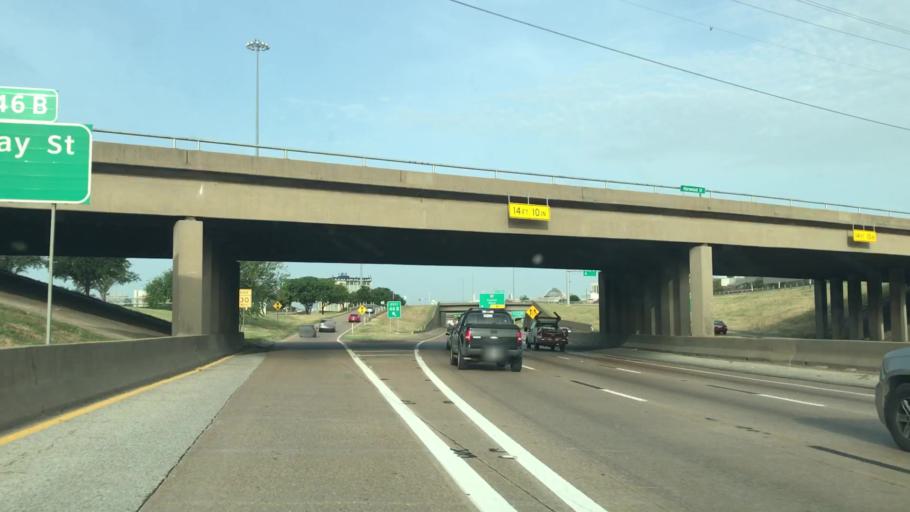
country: US
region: Texas
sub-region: Dallas County
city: Dallas
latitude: 32.7753
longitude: -96.7877
